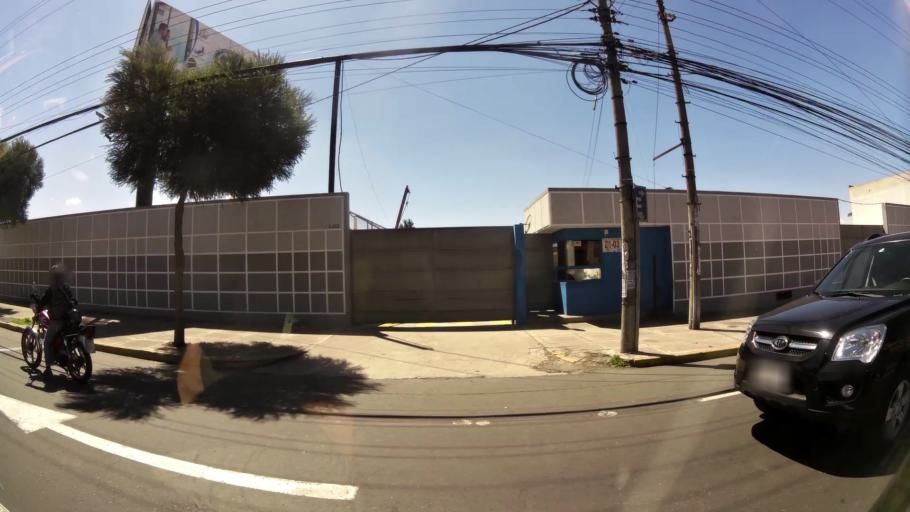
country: EC
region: Pichincha
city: Quito
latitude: -0.1429
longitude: -78.4922
